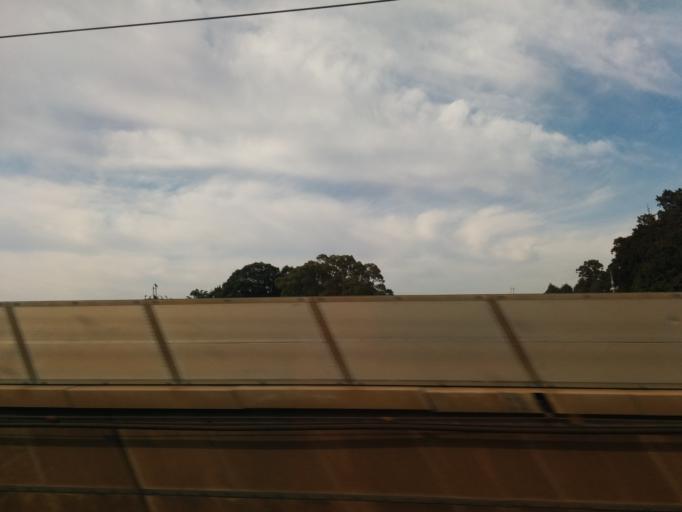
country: JP
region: Shiga Prefecture
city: Omihachiman
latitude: 35.1133
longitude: 136.1184
